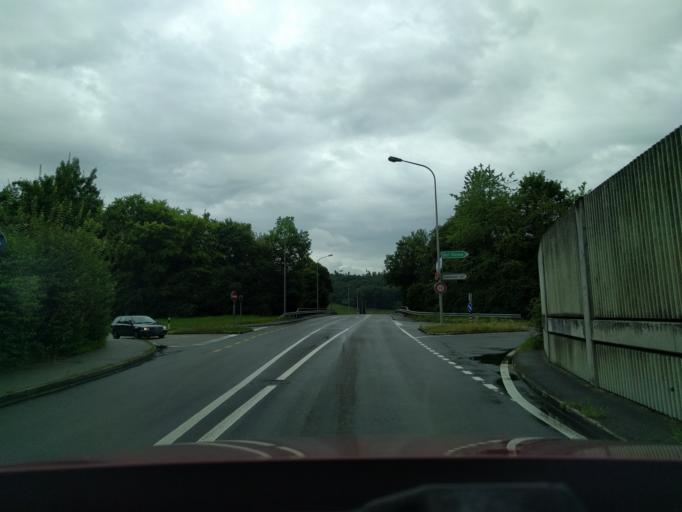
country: CH
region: Bern
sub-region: Bern-Mittelland District
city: Munchenbuchsee
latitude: 47.0389
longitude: 7.4301
